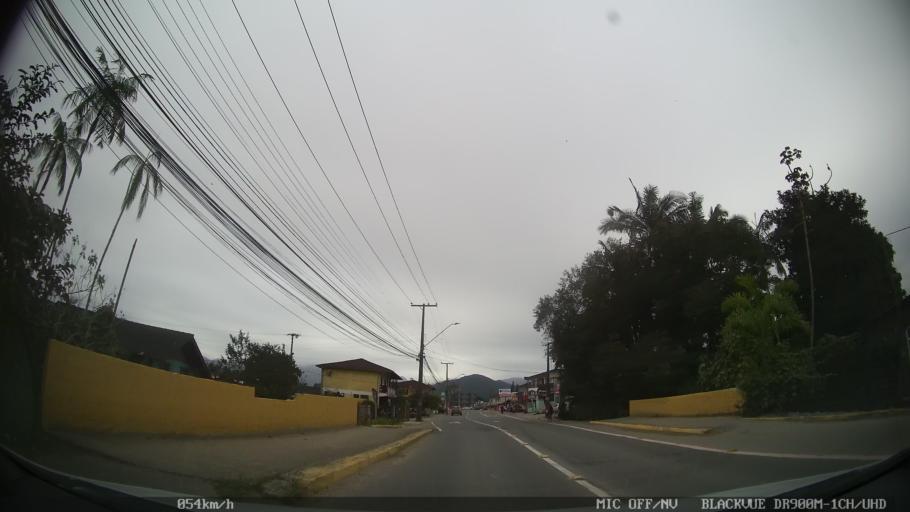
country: BR
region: Santa Catarina
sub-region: Joinville
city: Joinville
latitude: -26.2881
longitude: -48.8966
